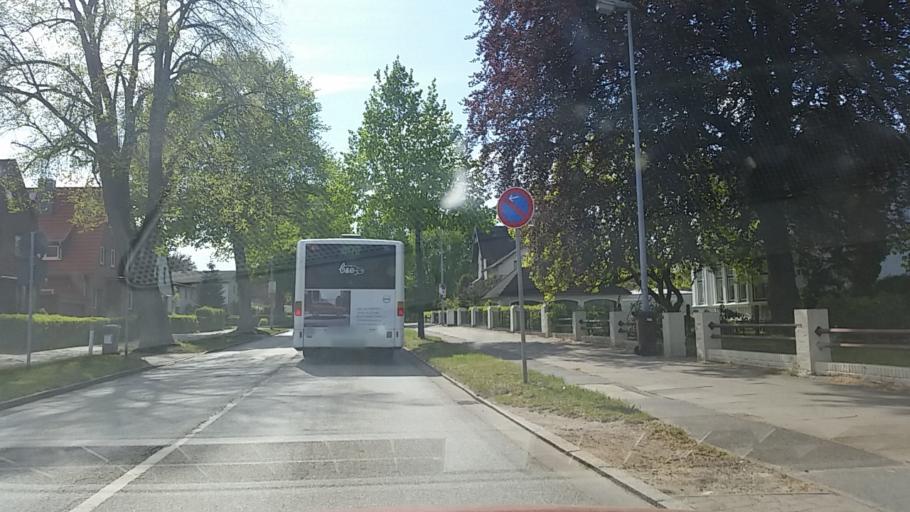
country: DE
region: Schleswig-Holstein
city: Bad Oldesloe
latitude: 53.8132
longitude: 10.3898
